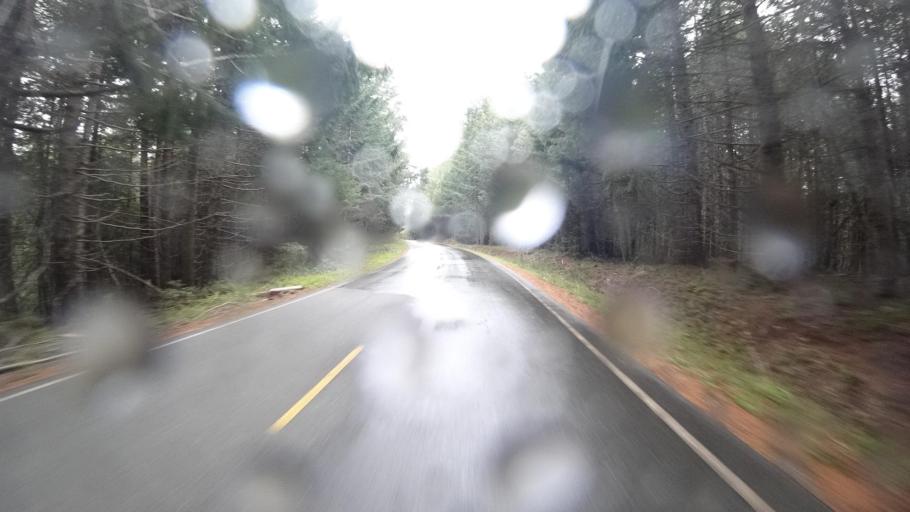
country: US
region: California
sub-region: Humboldt County
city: Willow Creek
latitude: 41.1939
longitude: -123.8109
